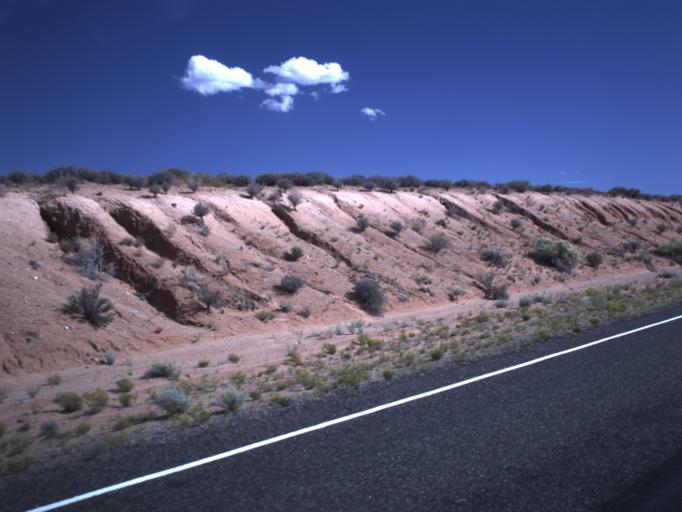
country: US
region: Utah
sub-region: Wayne County
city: Loa
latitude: 38.1634
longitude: -110.6226
